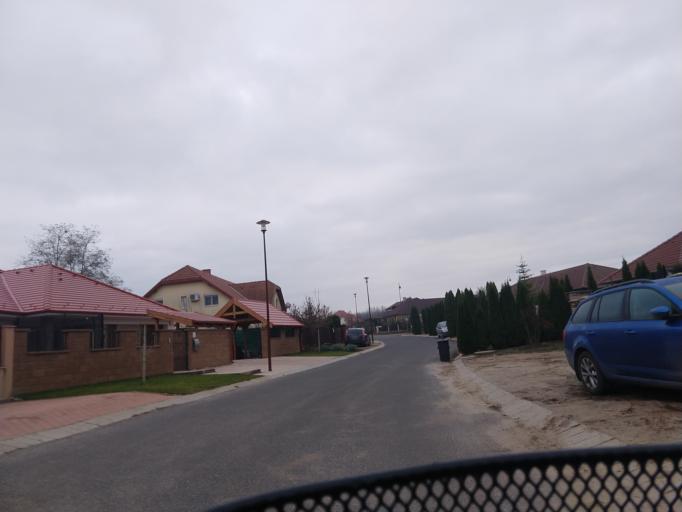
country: HU
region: Pest
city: Orbottyan
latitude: 47.6609
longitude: 19.2547
